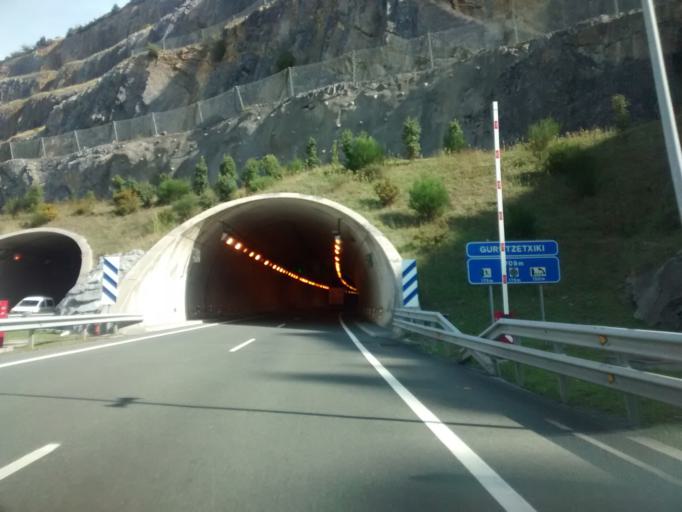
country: ES
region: Basque Country
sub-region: Provincia de Guipuzcoa
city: Arrasate / Mondragon
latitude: 43.0553
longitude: -2.4890
